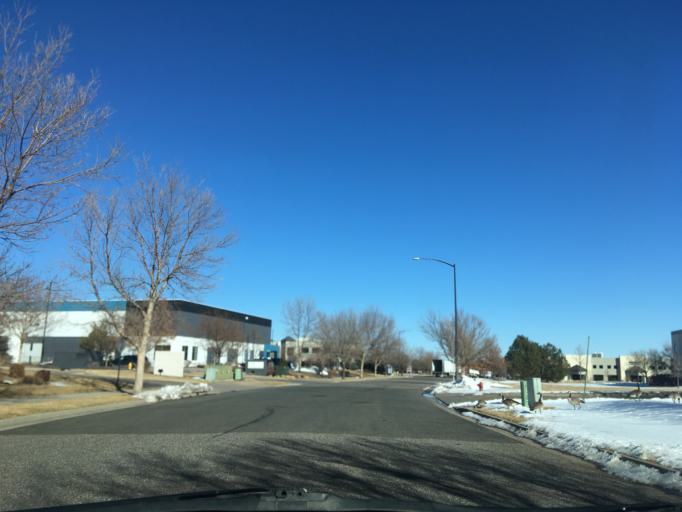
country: US
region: Colorado
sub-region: Boulder County
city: Louisville
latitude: 39.9674
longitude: -105.1146
